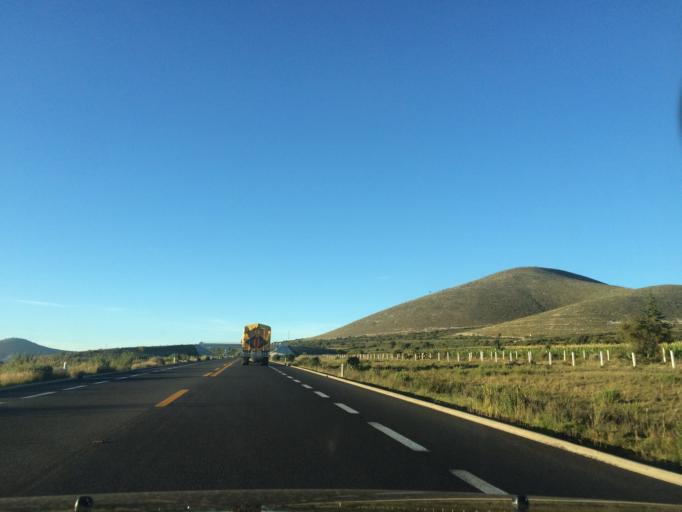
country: MX
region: Puebla
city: Morelos Canada
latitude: 18.7322
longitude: -97.4754
